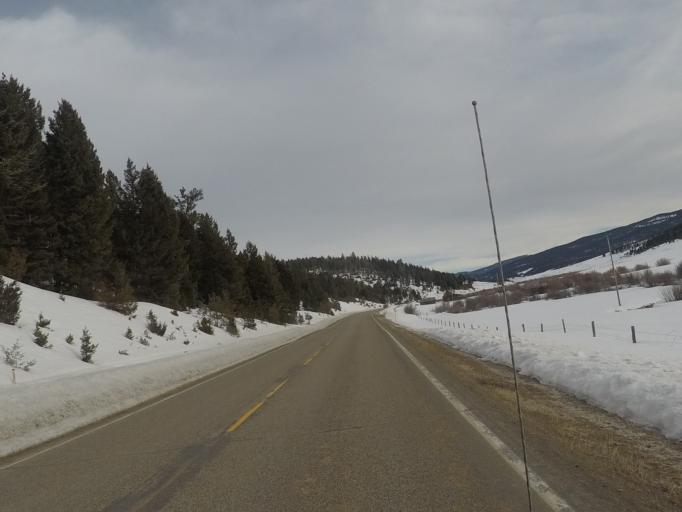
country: US
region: Montana
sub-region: Meagher County
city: White Sulphur Springs
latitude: 46.7031
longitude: -110.8626
